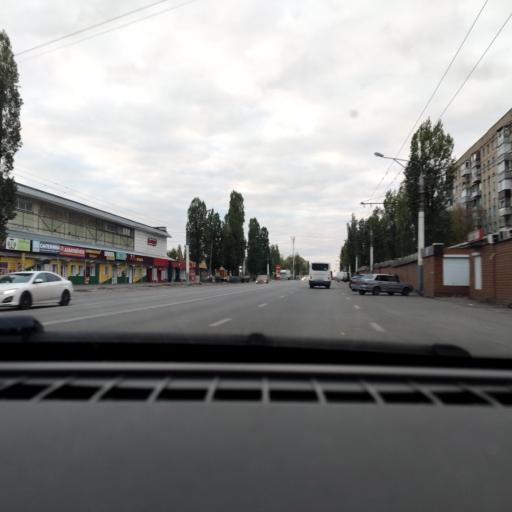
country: RU
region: Voronezj
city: Maslovka
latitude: 51.6126
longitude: 39.2372
